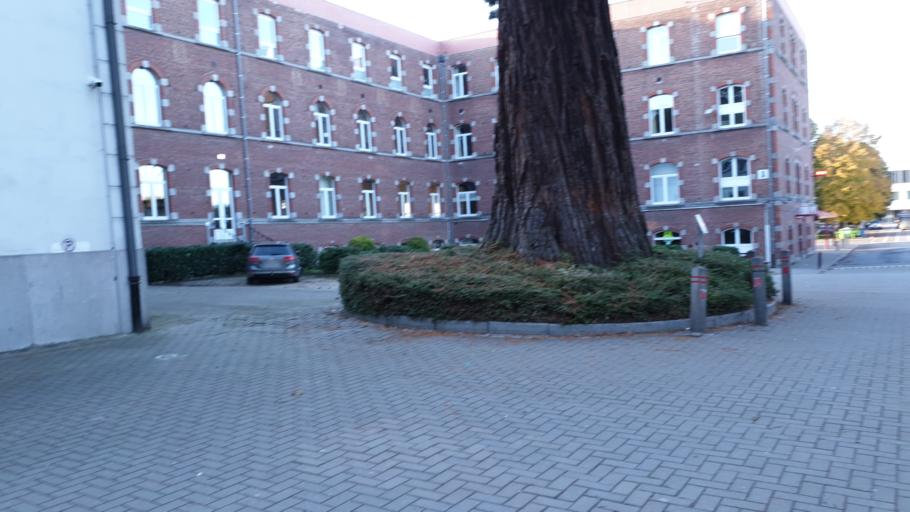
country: BE
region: Flanders
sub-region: Provincie Vlaams-Brabant
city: Halle
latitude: 50.7433
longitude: 4.2290
